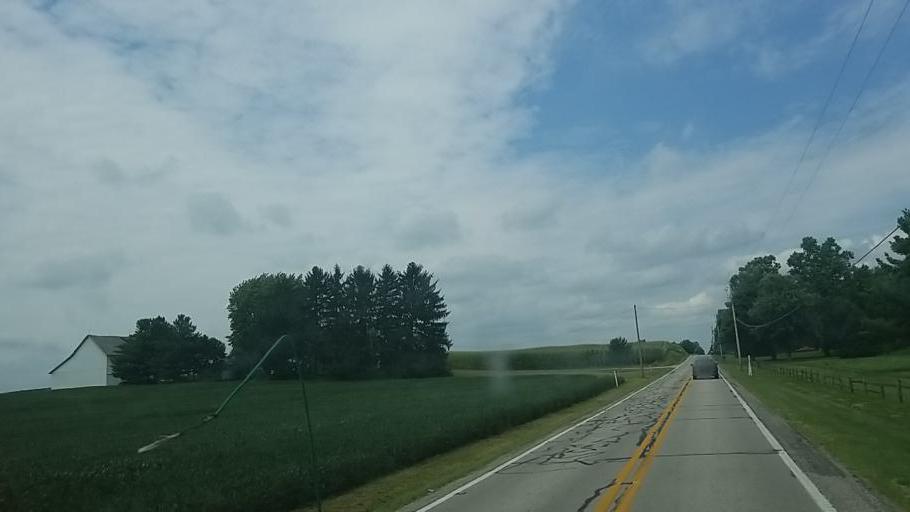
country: US
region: Ohio
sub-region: Fairfield County
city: Lithopolis
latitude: 39.7978
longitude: -82.8714
